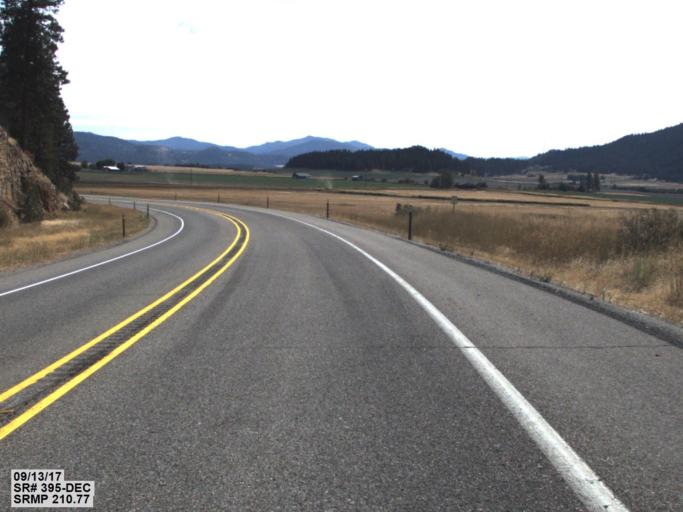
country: US
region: Washington
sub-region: Stevens County
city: Chewelah
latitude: 48.3042
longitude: -117.7757
